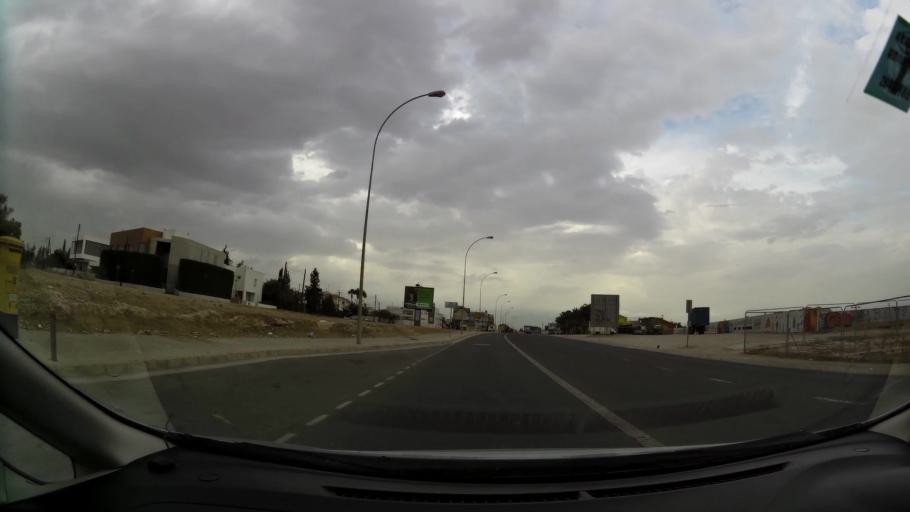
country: CY
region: Lefkosia
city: Nicosia
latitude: 35.1289
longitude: 33.3565
